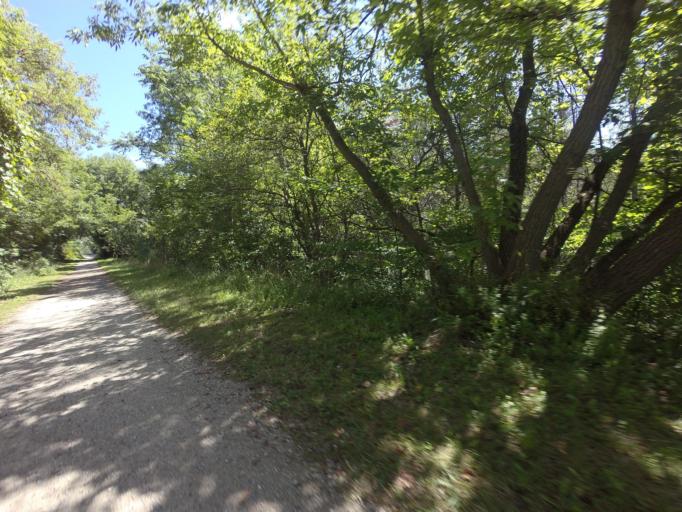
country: CA
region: Ontario
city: Orangeville
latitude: 43.7847
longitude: -80.1375
